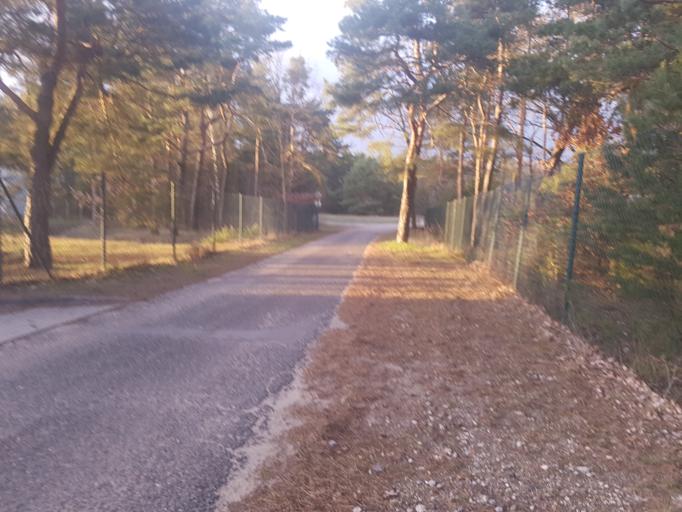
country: DE
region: Brandenburg
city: Eisenhuettenstadt
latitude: 52.1594
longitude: 14.6644
